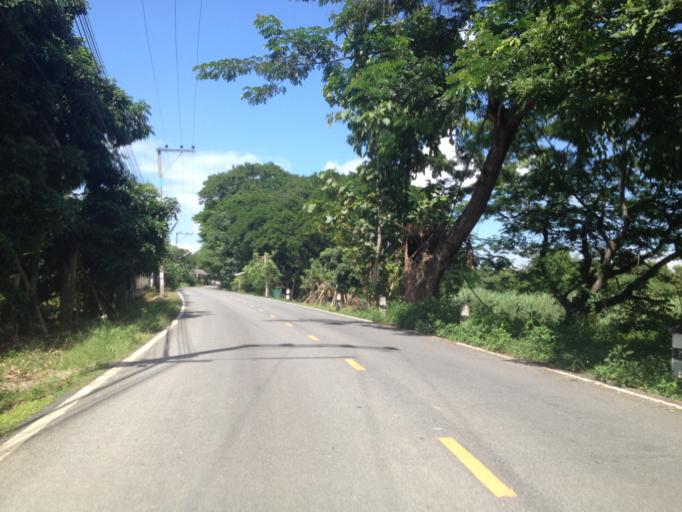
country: TH
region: Chiang Mai
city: Hang Dong
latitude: 18.6725
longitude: 98.9709
